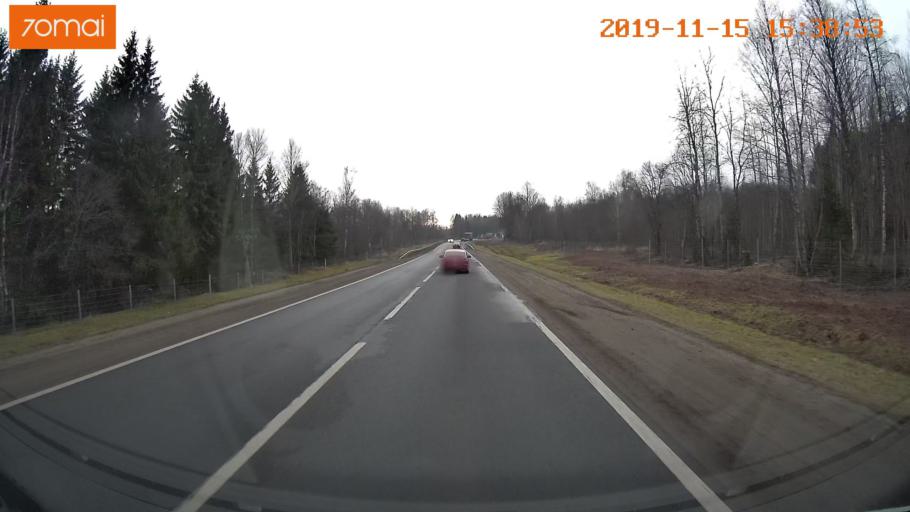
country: RU
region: Jaroslavl
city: Danilov
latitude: 58.0258
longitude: 40.0752
